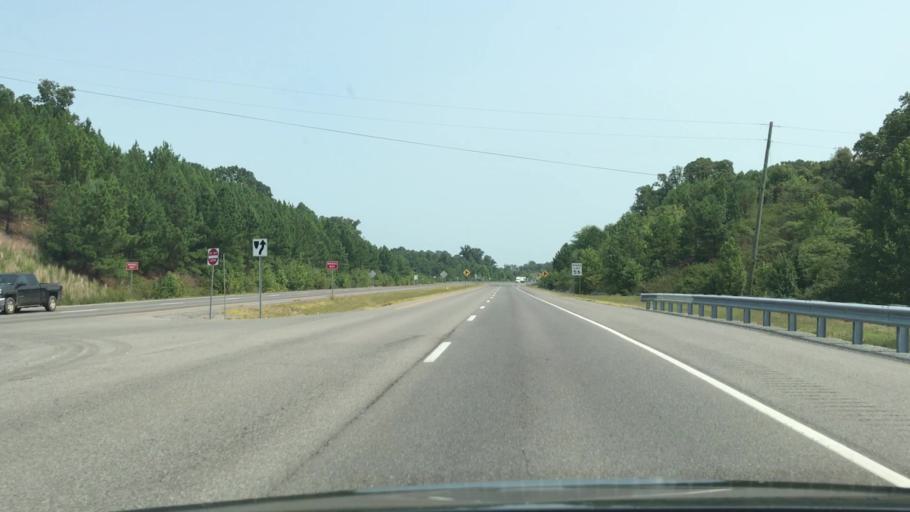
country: US
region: Kentucky
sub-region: Calloway County
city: Murray
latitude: 36.7588
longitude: -88.1502
